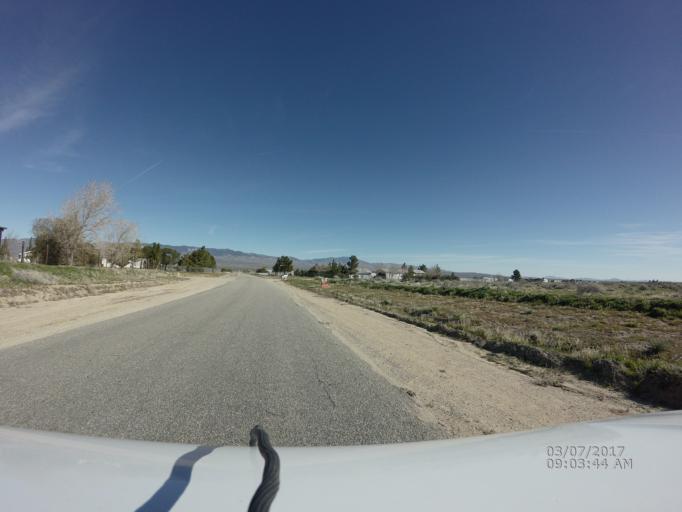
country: US
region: California
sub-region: Los Angeles County
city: Green Valley
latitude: 34.7885
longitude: -118.5813
